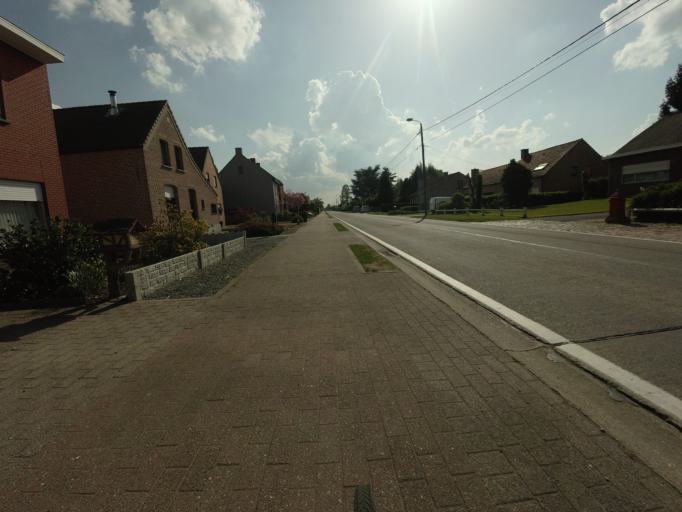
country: BE
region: Flanders
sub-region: Provincie Antwerpen
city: Putte
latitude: 51.0685
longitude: 4.6428
